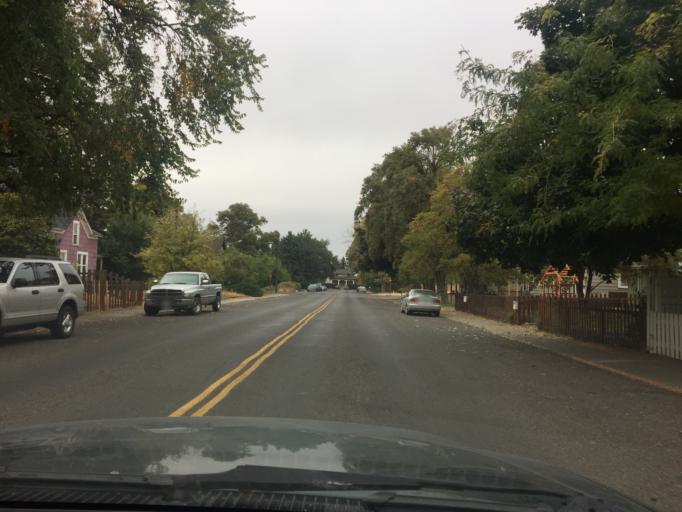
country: US
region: Washington
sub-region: Kittitas County
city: Ellensburg
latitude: 46.9903
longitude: -120.5443
